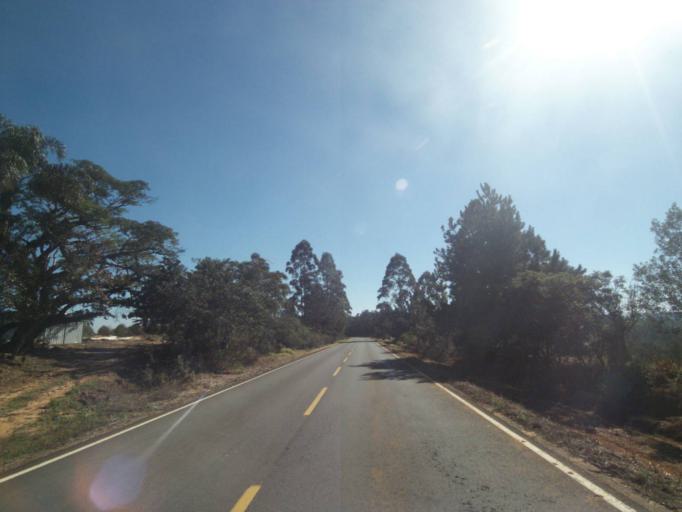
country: BR
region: Parana
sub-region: Tibagi
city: Tibagi
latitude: -24.4538
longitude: -50.5450
